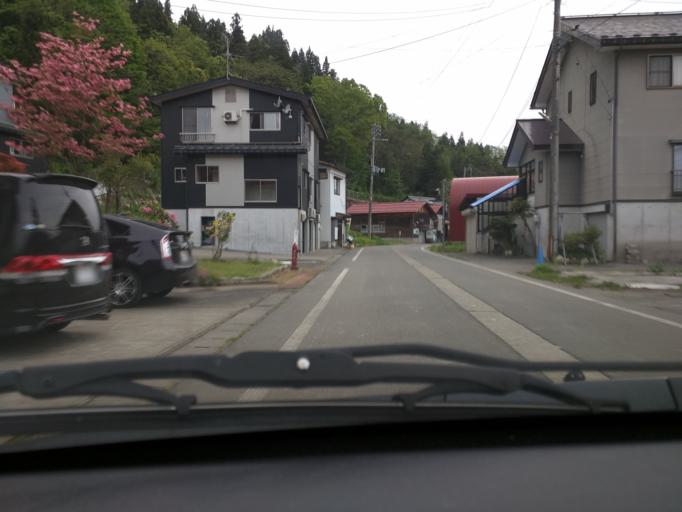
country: JP
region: Niigata
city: Muikamachi
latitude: 37.2128
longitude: 138.9504
